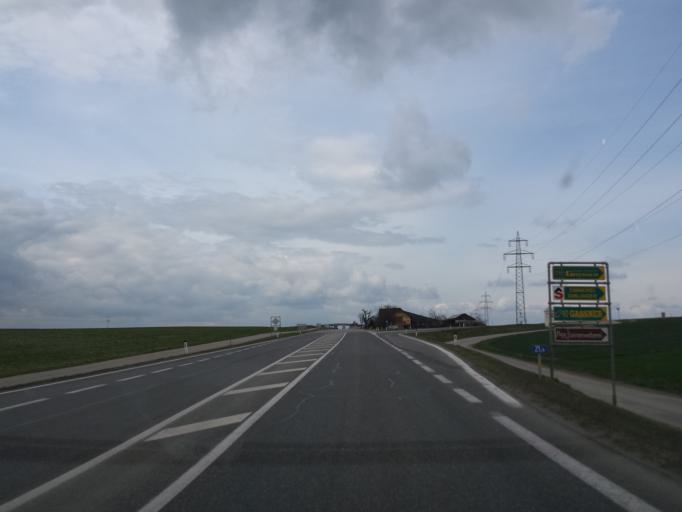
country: AT
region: Lower Austria
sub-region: Politischer Bezirk Krems
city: Jaidhof
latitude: 48.5255
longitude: 15.4765
